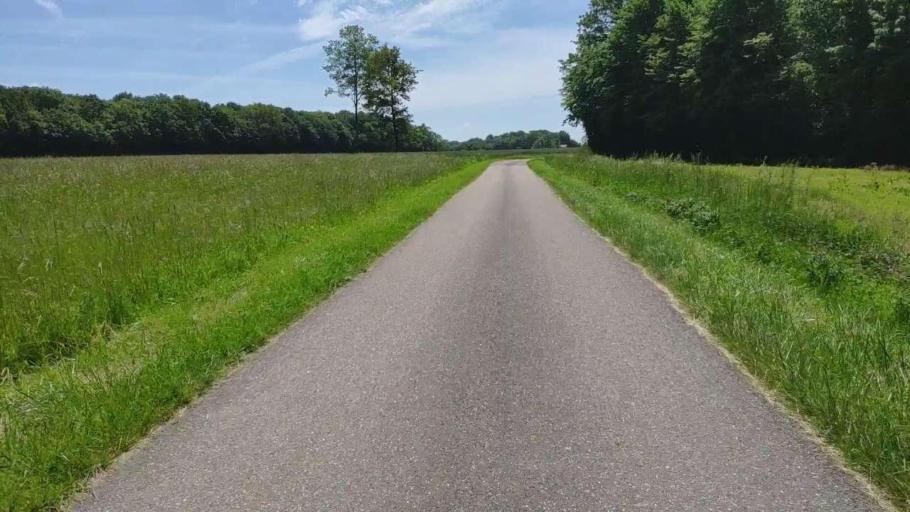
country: FR
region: Franche-Comte
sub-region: Departement du Jura
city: Bletterans
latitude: 46.7755
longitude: 5.3748
